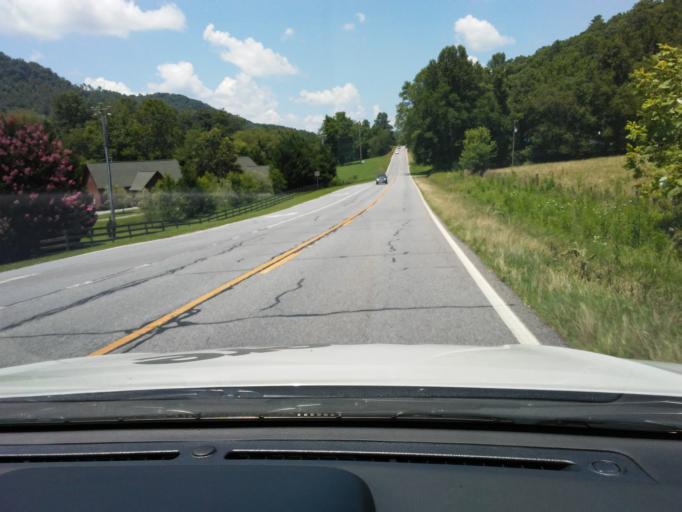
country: US
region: Georgia
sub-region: Towns County
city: Hiawassee
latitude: 34.8958
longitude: -83.7205
